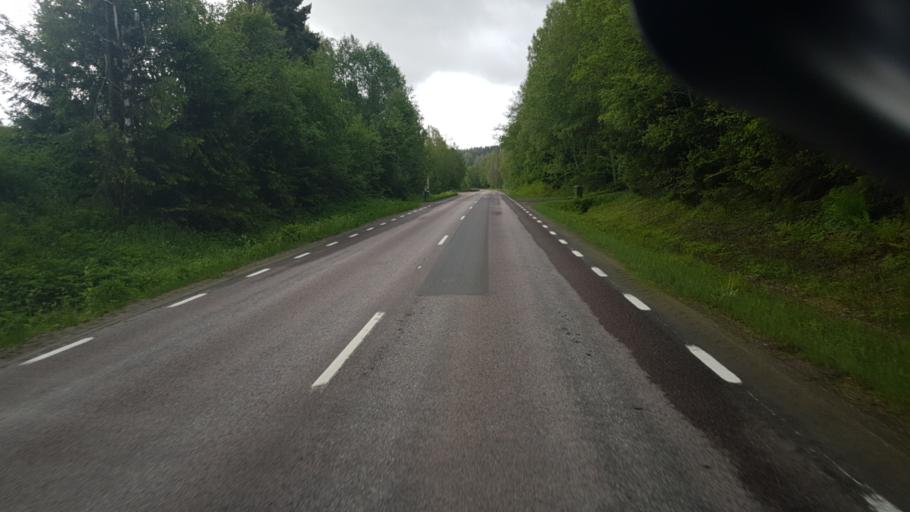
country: SE
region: Vaermland
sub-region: Eda Kommun
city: Amotfors
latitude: 59.6884
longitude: 12.3516
